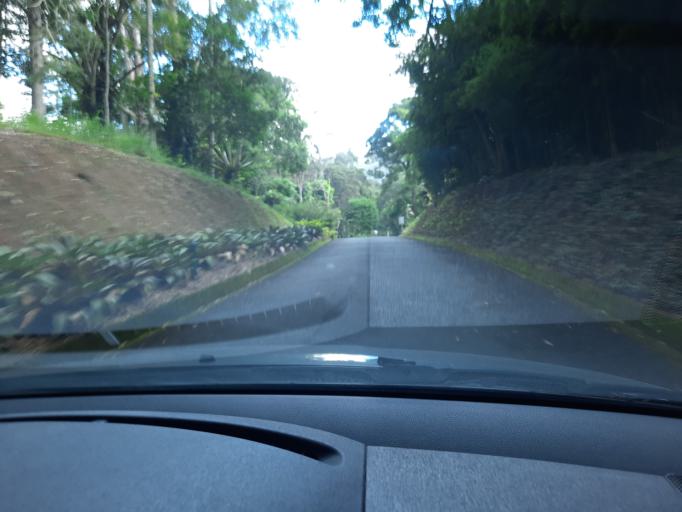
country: BR
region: Rio de Janeiro
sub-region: Petropolis
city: Petropolis
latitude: -22.4350
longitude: -43.1735
